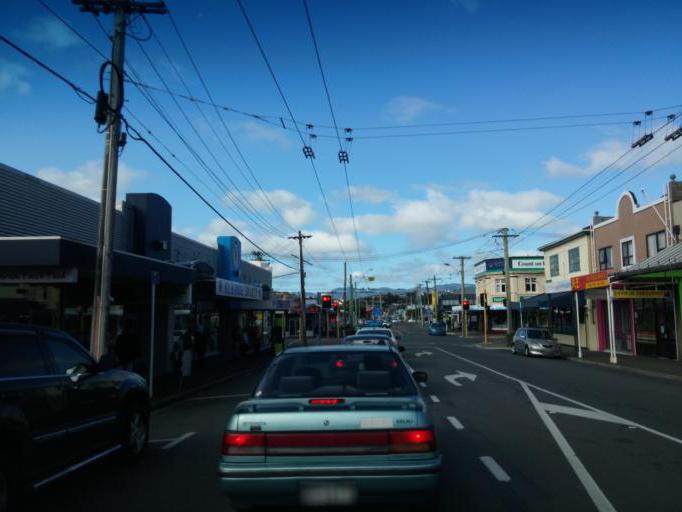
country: NZ
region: Wellington
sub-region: Wellington City
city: Wellington
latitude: -41.3178
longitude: 174.7944
